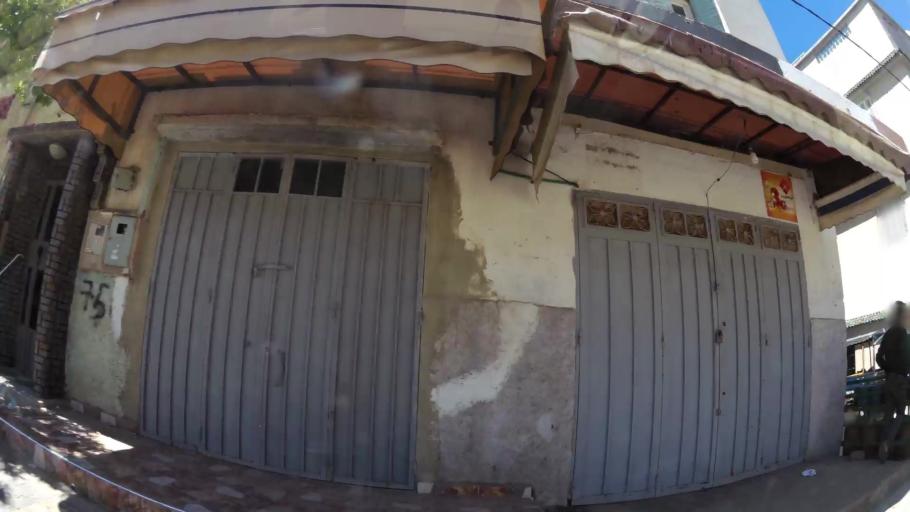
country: MA
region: Meknes-Tafilalet
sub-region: Meknes
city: Meknes
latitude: 33.8992
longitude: -5.5767
